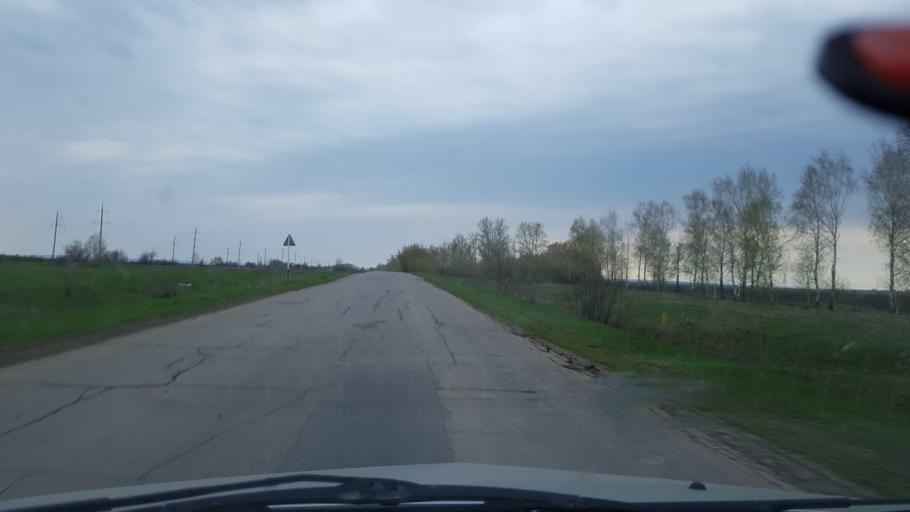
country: RU
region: Samara
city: Podstepki
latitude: 53.6675
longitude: 49.1498
